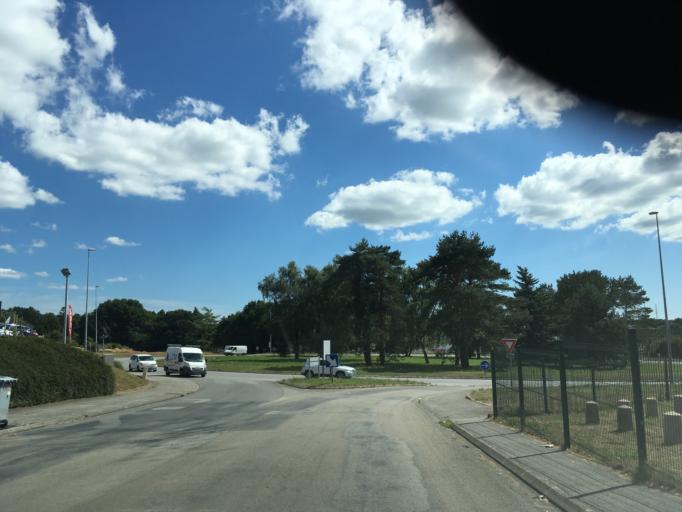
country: FR
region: Brittany
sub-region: Departement du Finistere
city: Ergue-Gaberic
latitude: 47.9822
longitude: -4.0341
